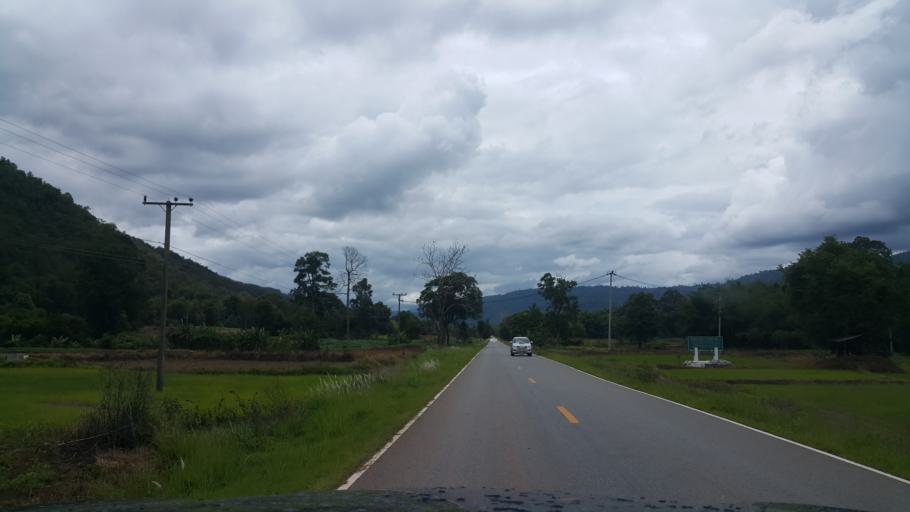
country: TH
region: Phitsanulok
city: Chat Trakan
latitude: 17.3191
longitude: 100.6818
